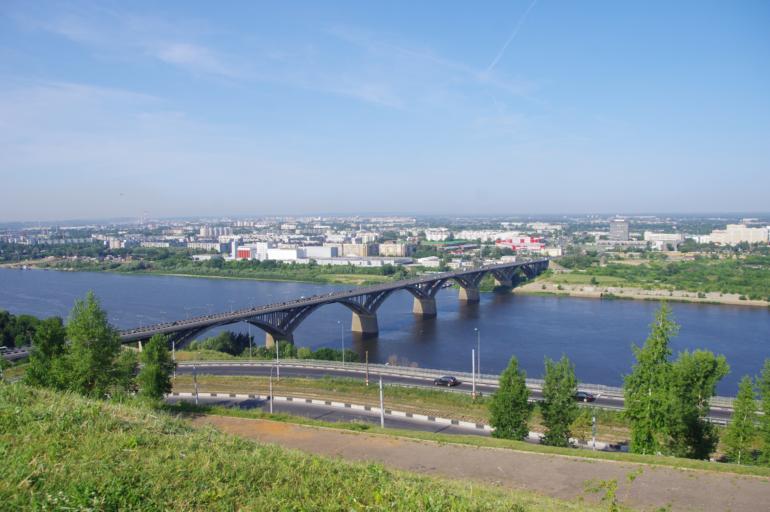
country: RU
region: Nizjnij Novgorod
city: Nizhniy Novgorod
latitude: 56.3020
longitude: 43.9722
